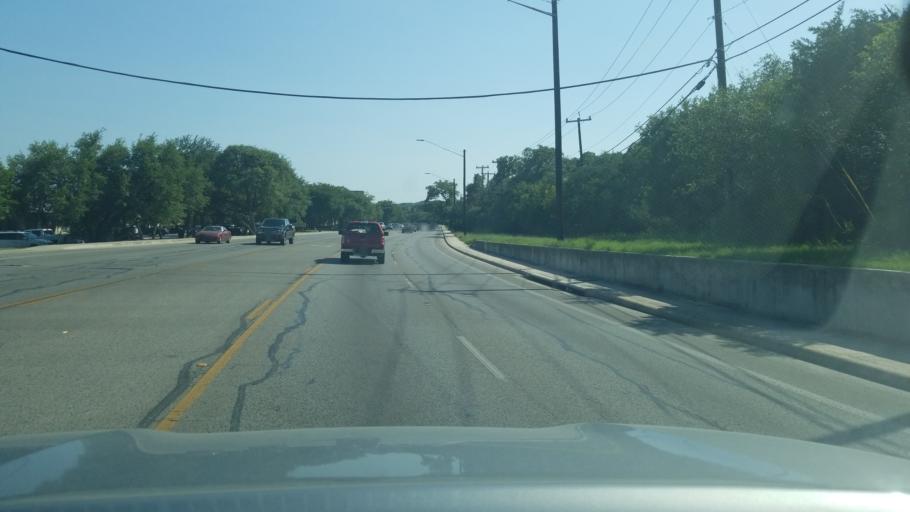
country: US
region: Texas
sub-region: Bexar County
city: Hollywood Park
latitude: 29.5907
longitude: -98.5125
